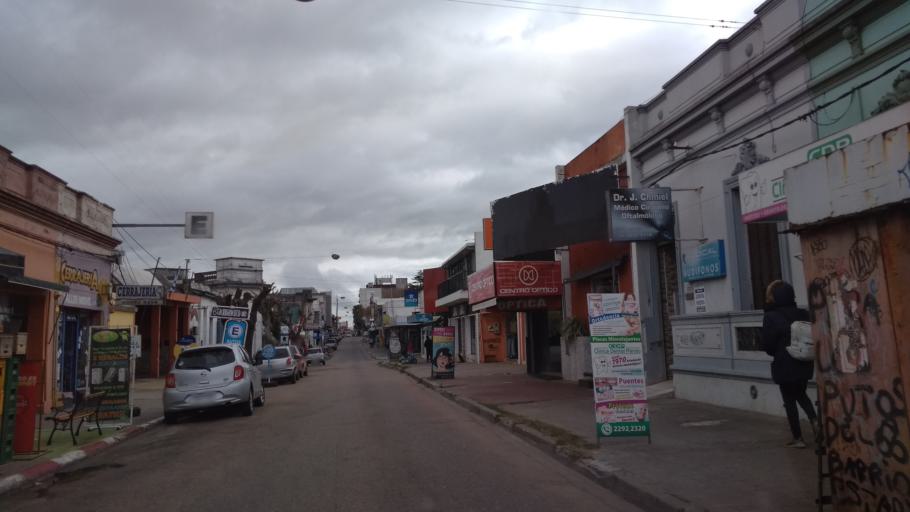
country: UY
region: Canelones
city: Pando
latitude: -34.7237
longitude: -55.9590
